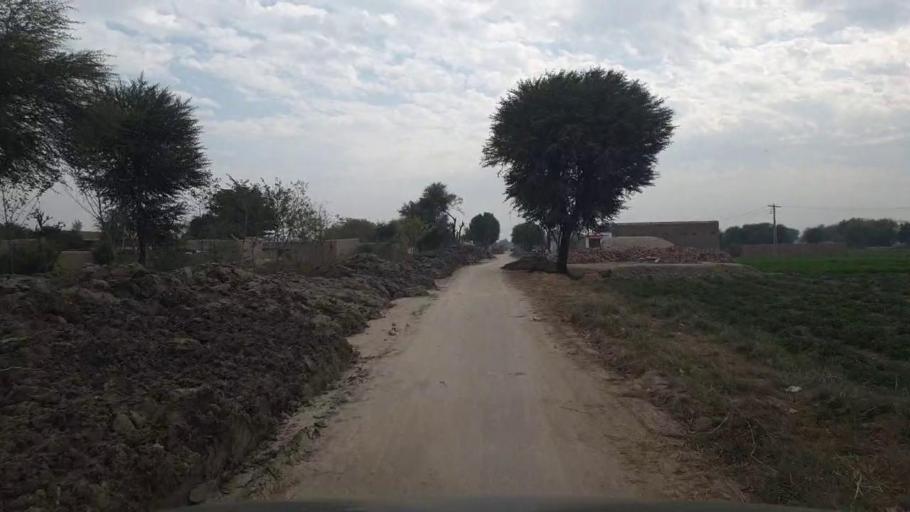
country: PK
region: Sindh
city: Sakrand
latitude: 26.0308
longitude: 68.4251
